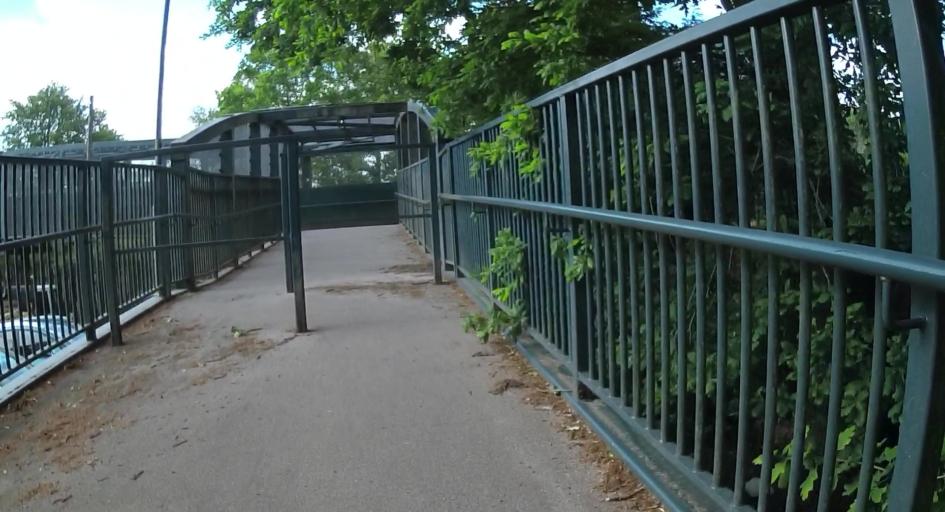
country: GB
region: England
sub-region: Hampshire
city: Fleet
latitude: 51.2890
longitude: -0.8480
